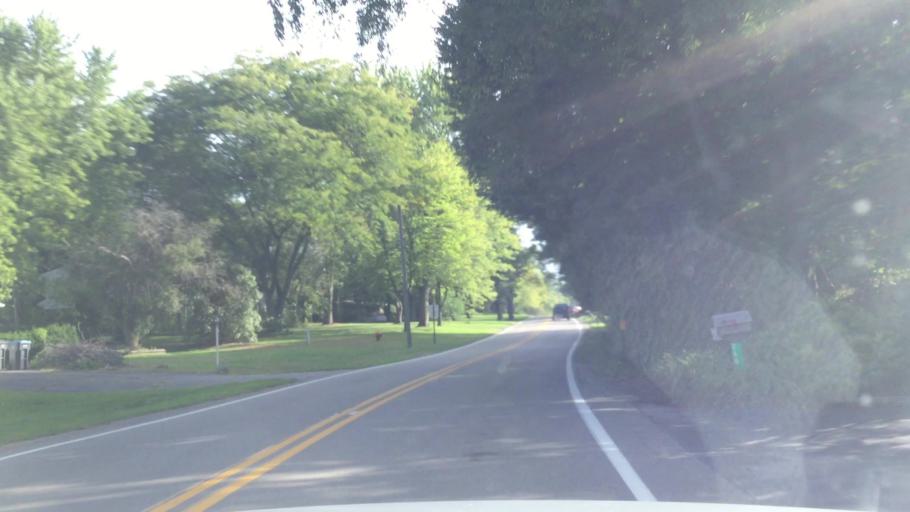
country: US
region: Michigan
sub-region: Livingston County
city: Howell
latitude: 42.6017
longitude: -83.9046
